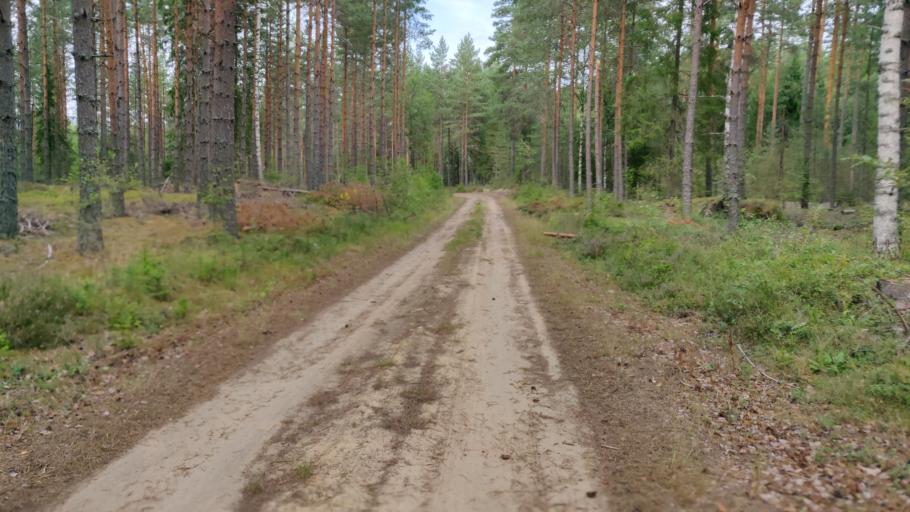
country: SE
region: Vaermland
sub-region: Hagfors Kommun
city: Hagfors
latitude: 60.0162
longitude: 13.5583
